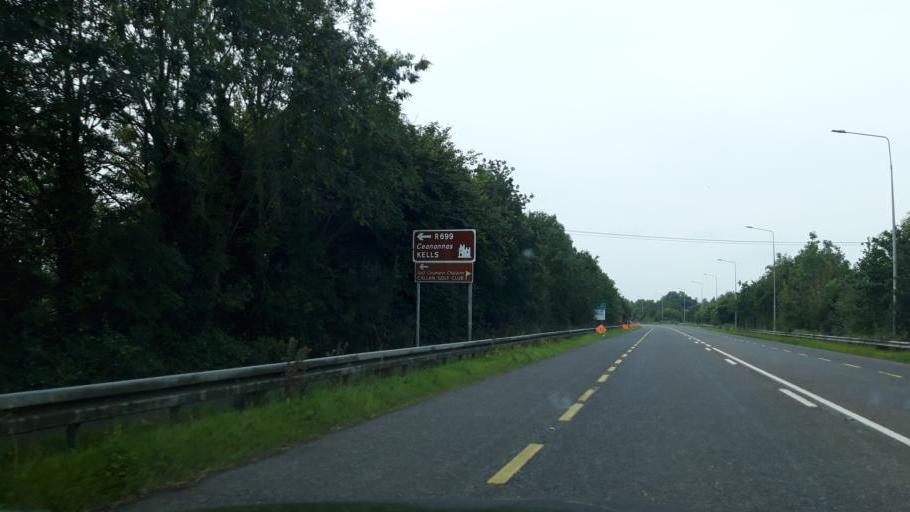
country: IE
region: Leinster
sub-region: Kilkenny
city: Callan
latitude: 52.5486
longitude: -7.3928
